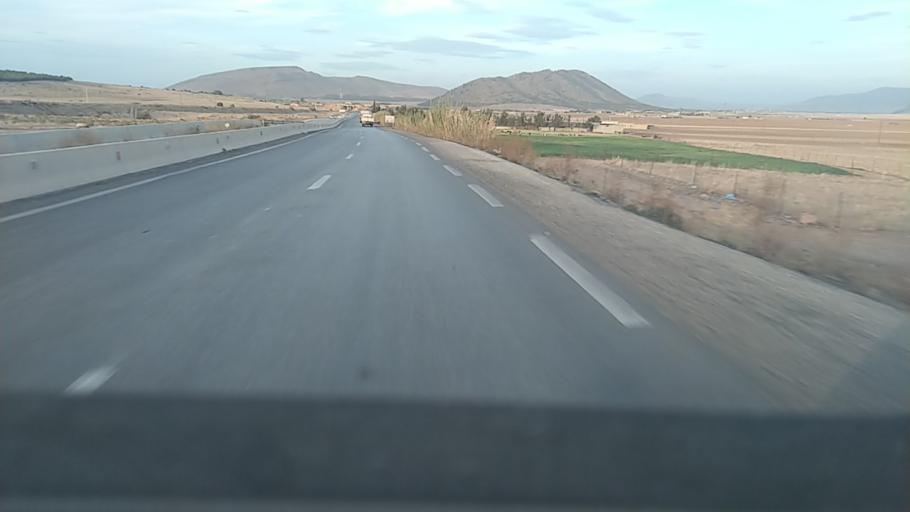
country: DZ
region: Oum el Bouaghi
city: Ain Kercha
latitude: 35.9455
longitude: 6.5229
